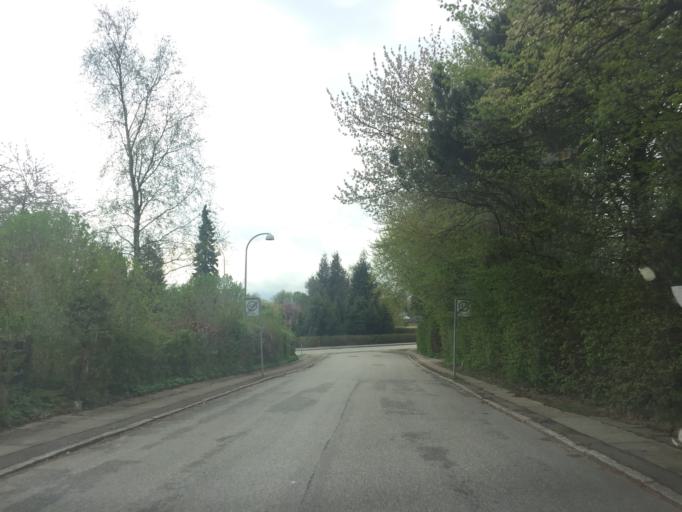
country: DK
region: Capital Region
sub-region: Herlev Kommune
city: Herlev
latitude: 55.7564
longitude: 12.4281
